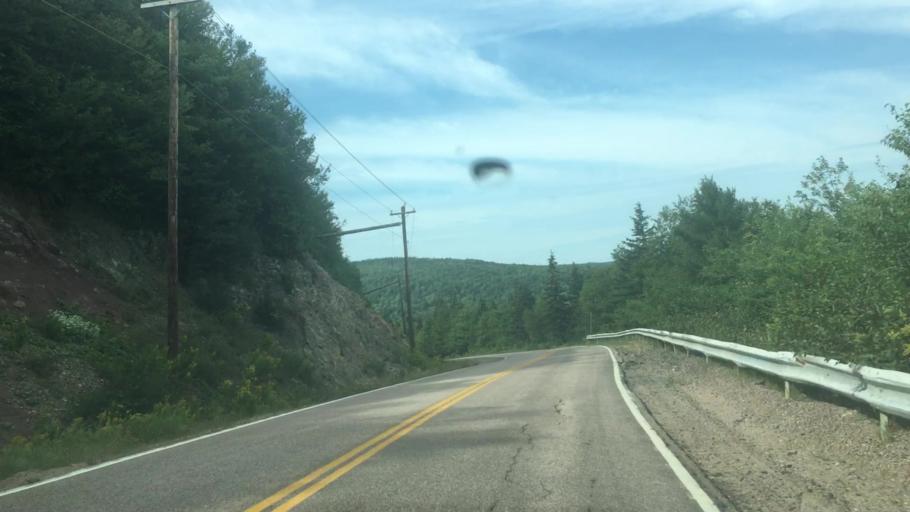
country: CA
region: Nova Scotia
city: Sydney Mines
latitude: 46.6031
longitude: -60.3857
